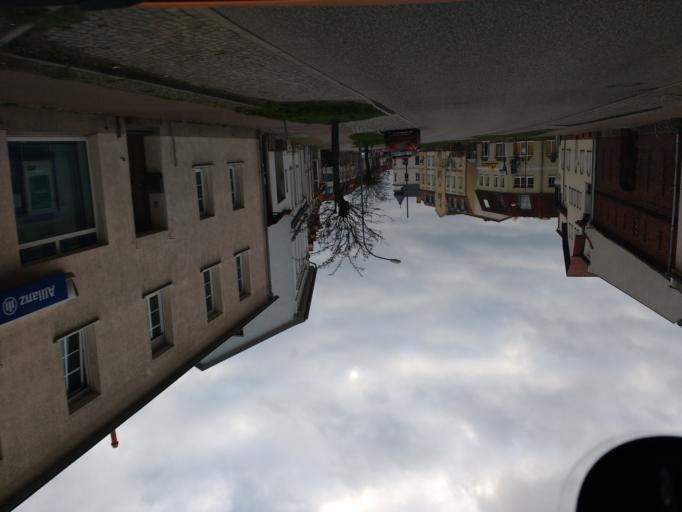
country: DE
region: Brandenburg
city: Wriezen
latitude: 52.7212
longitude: 14.1384
